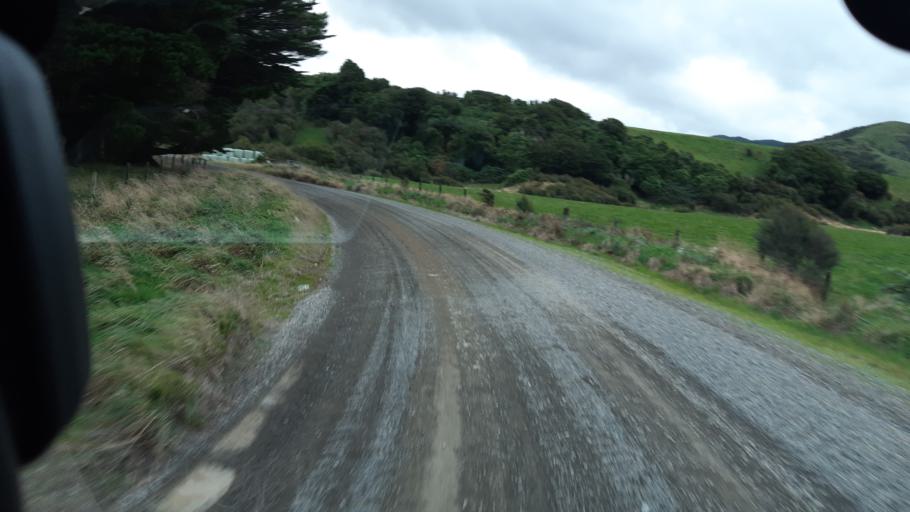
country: NZ
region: Manawatu-Wanganui
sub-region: Palmerston North City
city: Palmerston North
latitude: -40.6118
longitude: 175.6124
